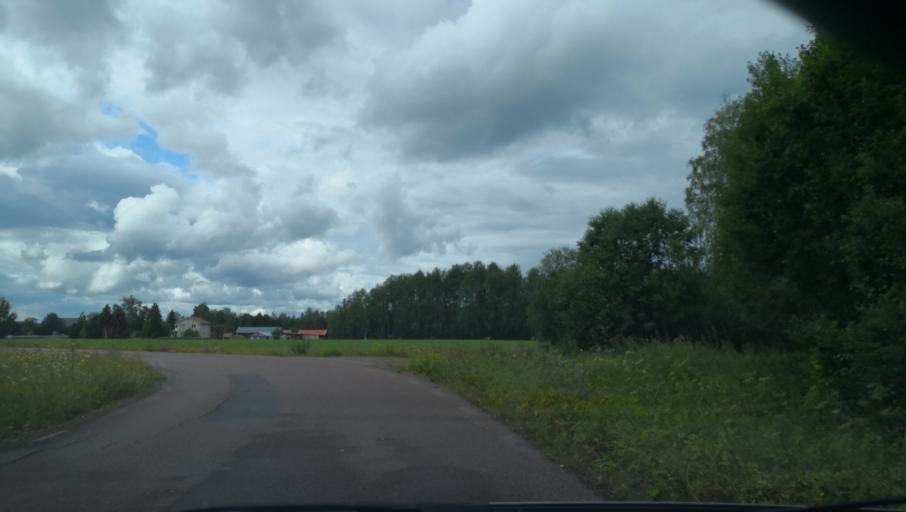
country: SE
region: Dalarna
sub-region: Borlange Kommun
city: Ornas
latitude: 60.4587
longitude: 15.5791
